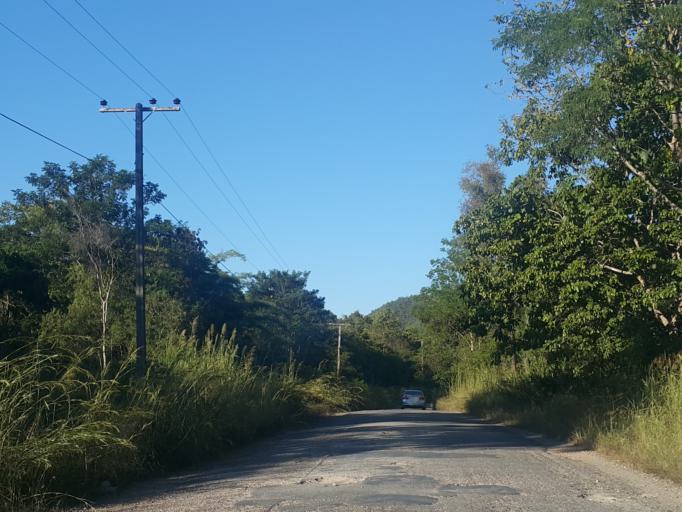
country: TH
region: Chiang Mai
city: San Sai
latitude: 18.9305
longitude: 99.1371
